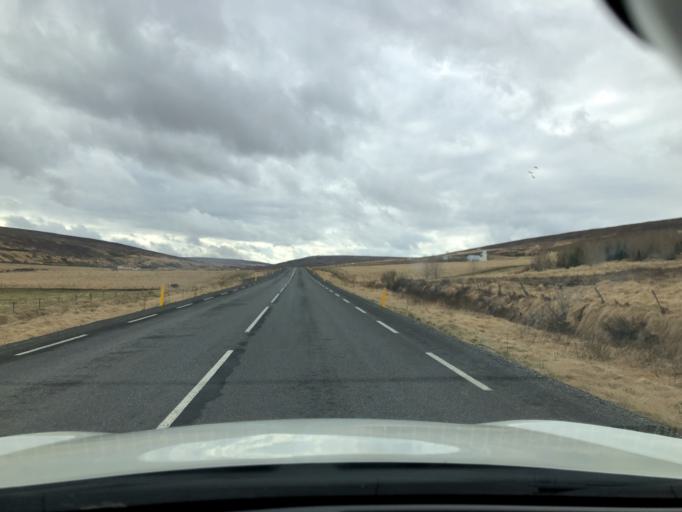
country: IS
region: Northeast
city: Laugar
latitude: 65.7119
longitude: -17.3646
